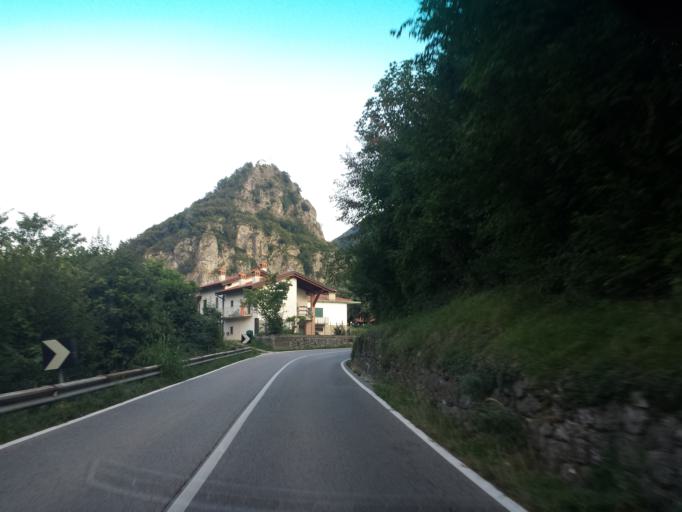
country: IT
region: Veneto
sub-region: Provincia di Vicenza
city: Cogollo del Cengio
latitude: 45.7800
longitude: 11.4003
